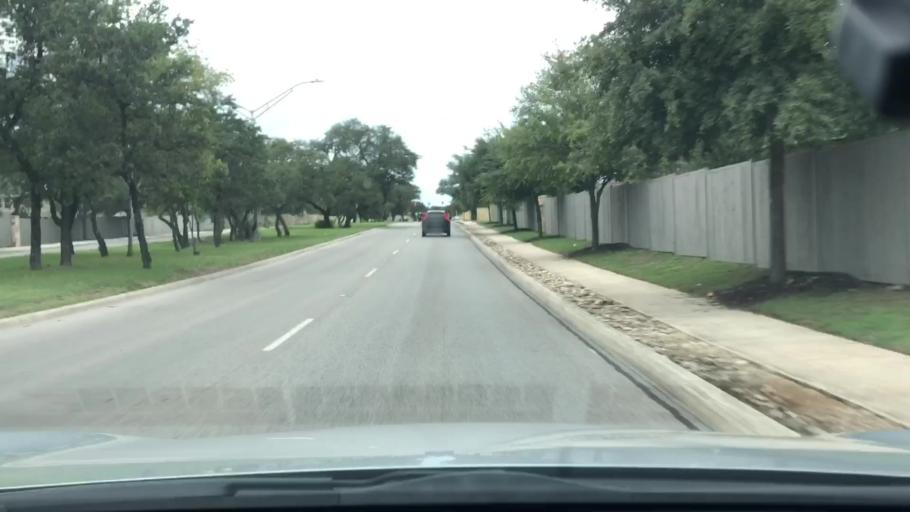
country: US
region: Texas
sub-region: Bexar County
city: Leon Valley
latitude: 29.4580
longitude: -98.6703
